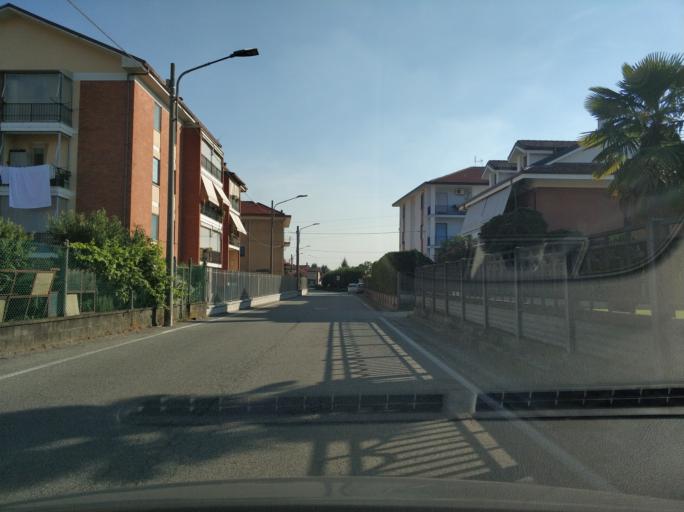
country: IT
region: Piedmont
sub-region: Provincia di Torino
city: San Maurizio
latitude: 45.2112
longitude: 7.6299
